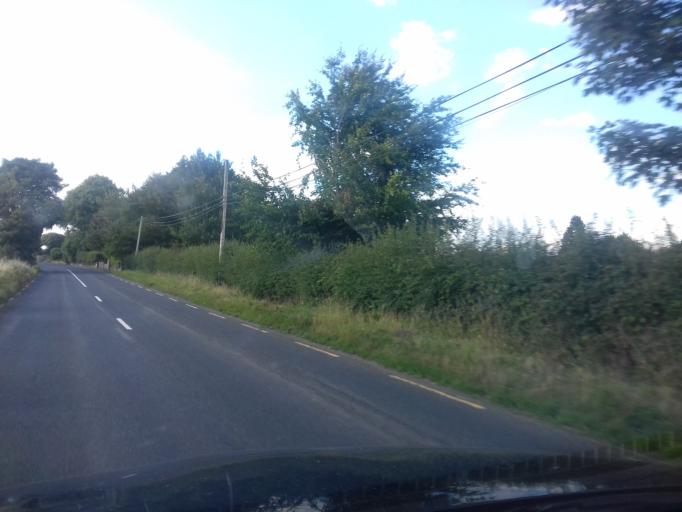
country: IE
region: Leinster
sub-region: Loch Garman
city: New Ross
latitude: 52.4430
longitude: -6.9612
